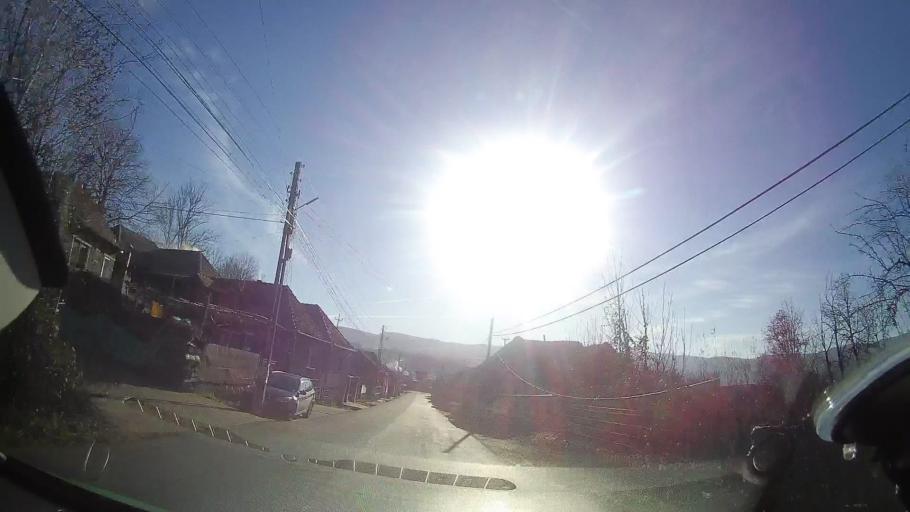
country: RO
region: Bihor
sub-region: Comuna Vadu Crisului
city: Vadu Crisului
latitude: 46.9921
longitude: 22.5220
